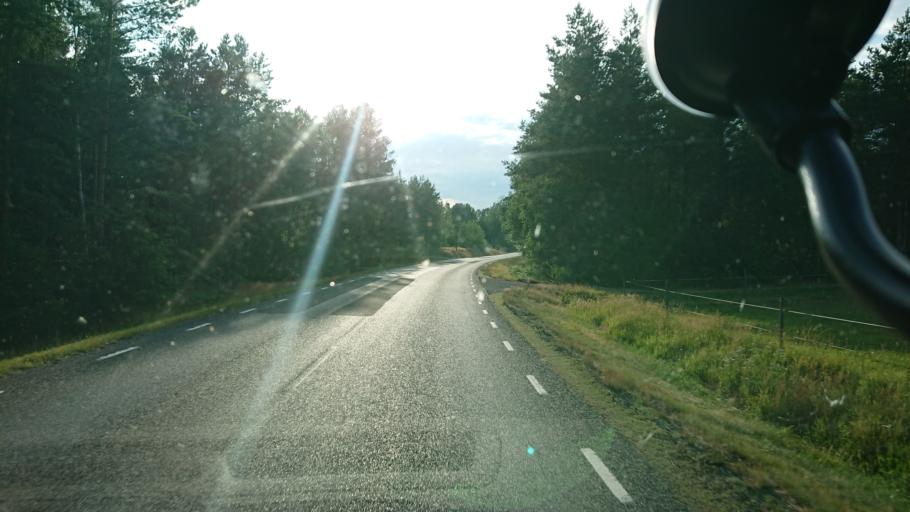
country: SE
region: Kronoberg
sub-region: Vaxjo Kommun
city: Rottne
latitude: 57.0334
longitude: 14.9499
